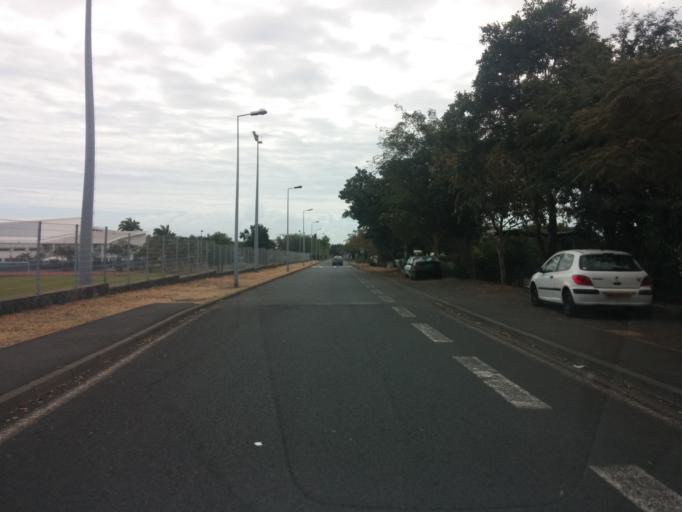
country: RE
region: Reunion
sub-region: Reunion
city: Le Port
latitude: -20.9511
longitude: 55.2944
